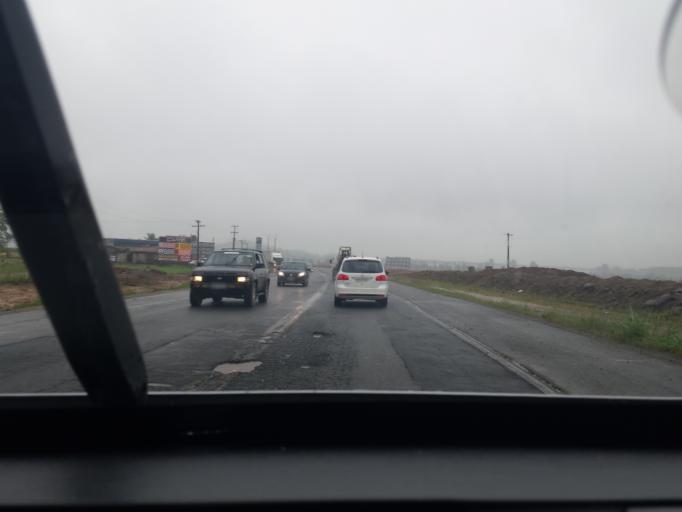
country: BR
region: Santa Catarina
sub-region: Navegantes
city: Navegantes
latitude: -26.8338
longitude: -48.7237
